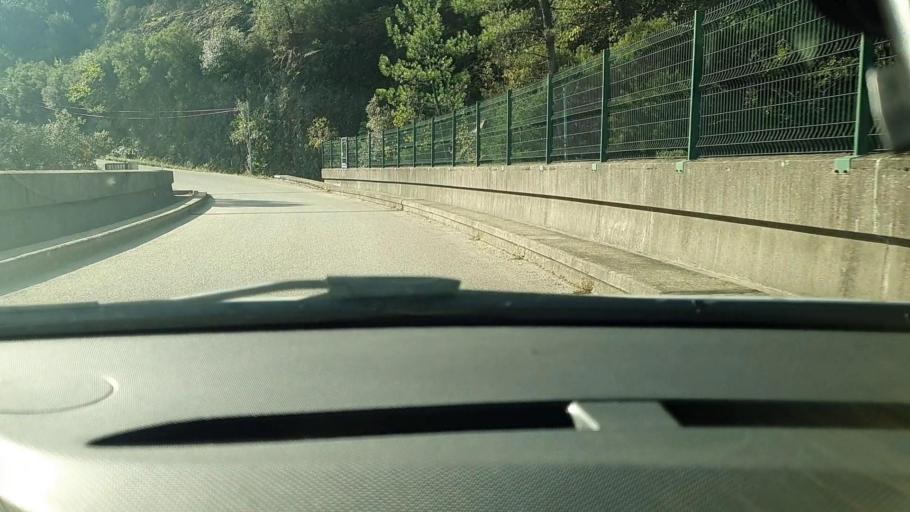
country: FR
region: Languedoc-Roussillon
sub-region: Departement du Gard
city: Besseges
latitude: 44.3184
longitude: 4.0479
